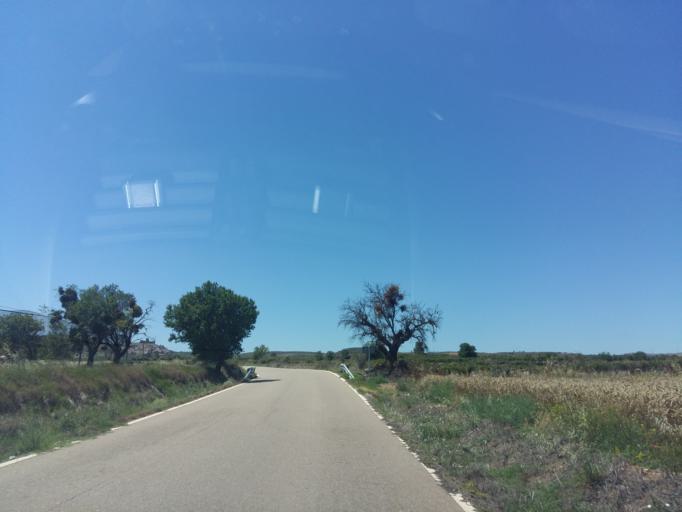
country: ES
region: Aragon
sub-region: Provincia de Zaragoza
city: Vera de Moncayo
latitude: 41.8273
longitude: -1.6968
